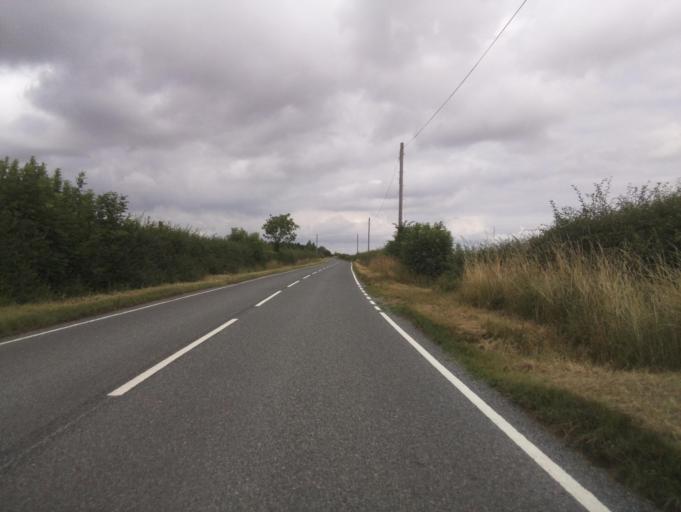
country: GB
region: England
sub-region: District of Rutland
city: Tickencote
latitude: 52.6769
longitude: -0.5136
